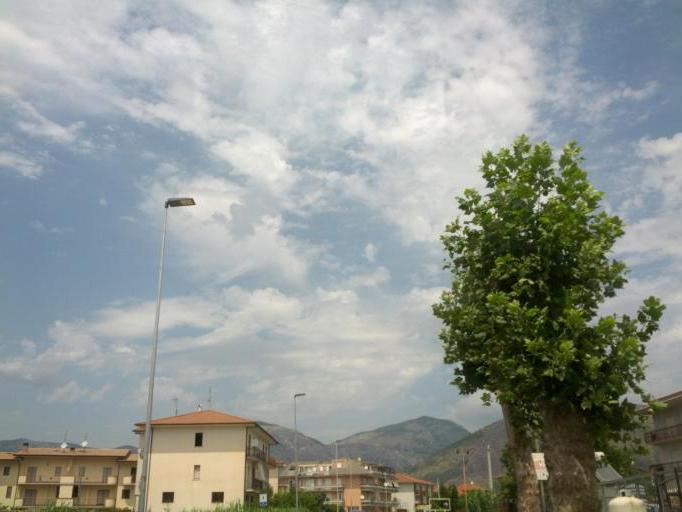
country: IT
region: Latium
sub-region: Provincia di Latina
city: Fondi
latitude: 41.3453
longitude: 13.4275
